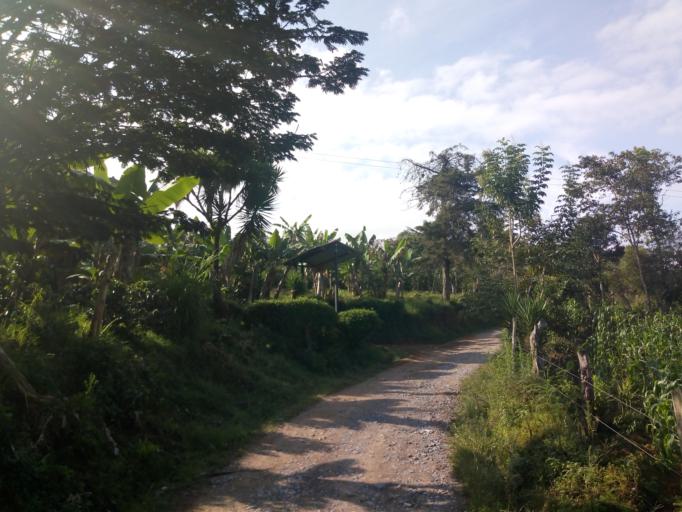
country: CO
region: Boyaca
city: Moniquira
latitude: 5.8874
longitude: -73.5236
